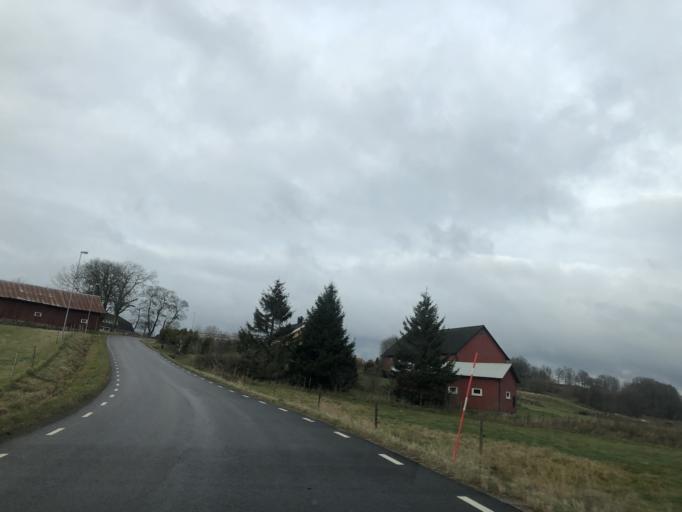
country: SE
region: Vaestra Goetaland
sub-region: Ulricehamns Kommun
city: Ulricehamn
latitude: 57.8219
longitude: 13.2456
